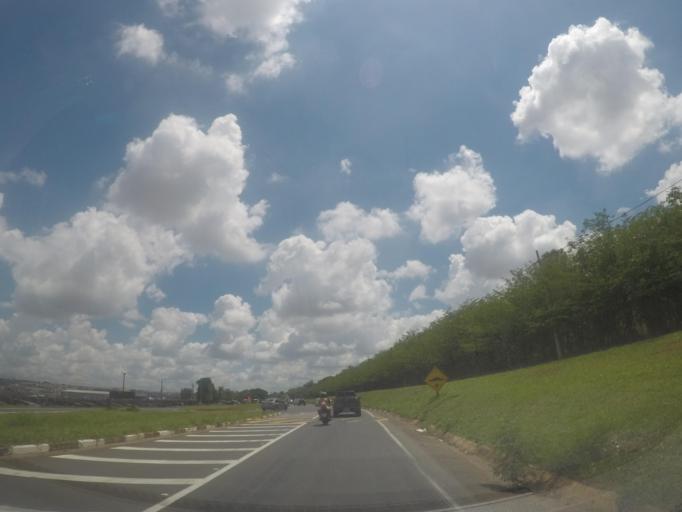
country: BR
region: Sao Paulo
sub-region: Hortolandia
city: Hortolandia
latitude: -22.8323
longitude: -47.2041
